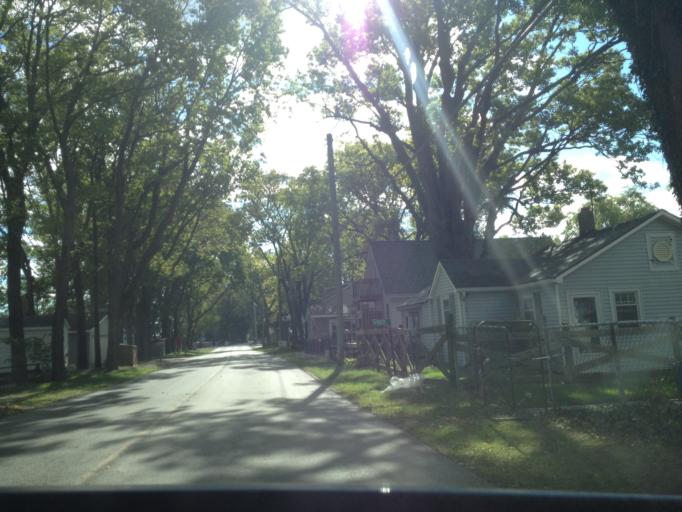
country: CA
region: Ontario
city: Amherstburg
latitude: 41.9919
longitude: -82.5539
